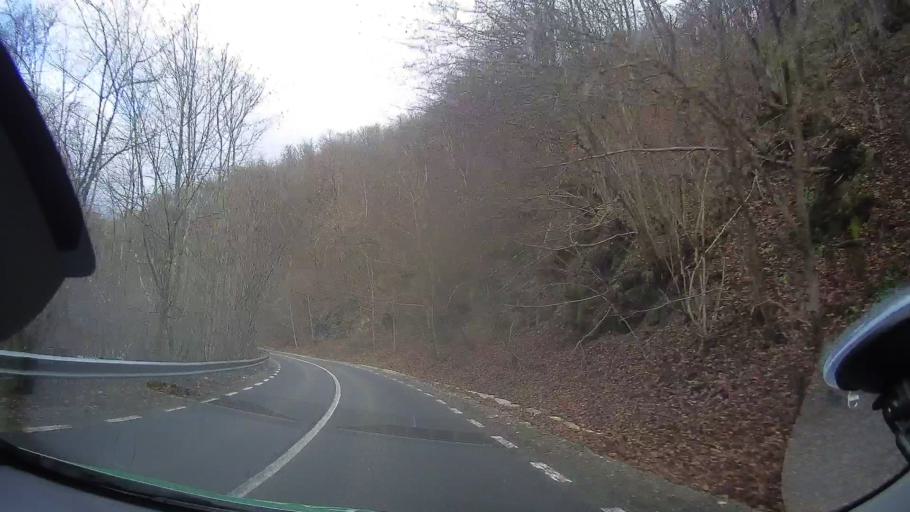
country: RO
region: Cluj
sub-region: Comuna Valea Ierii
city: Valea Ierii
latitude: 46.6314
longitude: 23.3744
